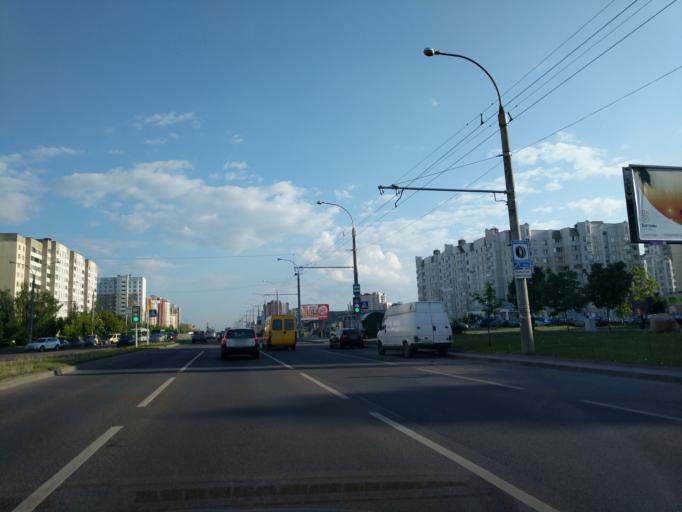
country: BY
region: Minsk
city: Novoye Medvezhino
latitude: 53.9123
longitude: 27.4363
